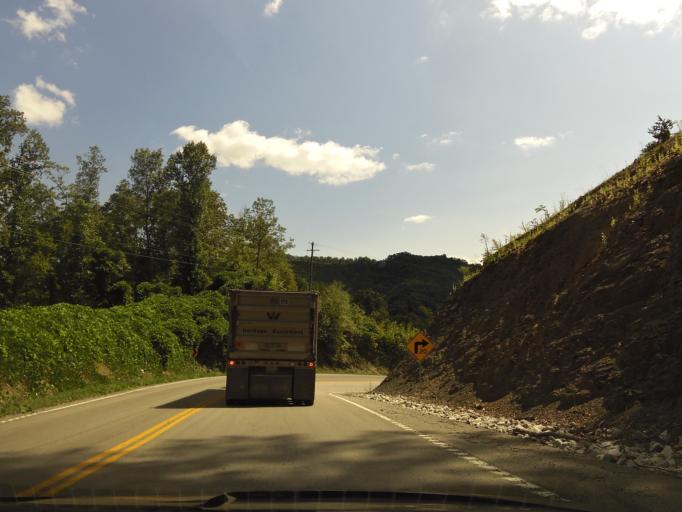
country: US
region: Kentucky
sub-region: Harlan County
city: Harlan
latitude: 36.8725
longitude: -83.3194
